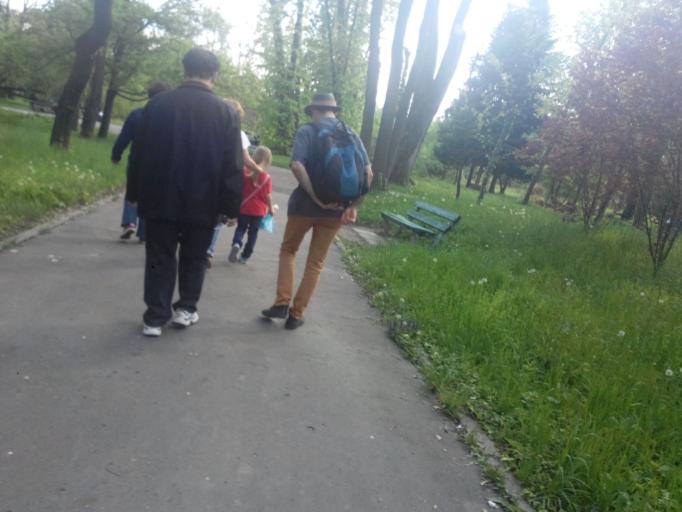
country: RO
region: Bucuresti
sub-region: Municipiul Bucuresti
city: Bucuresti
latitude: 44.4379
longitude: 26.0643
